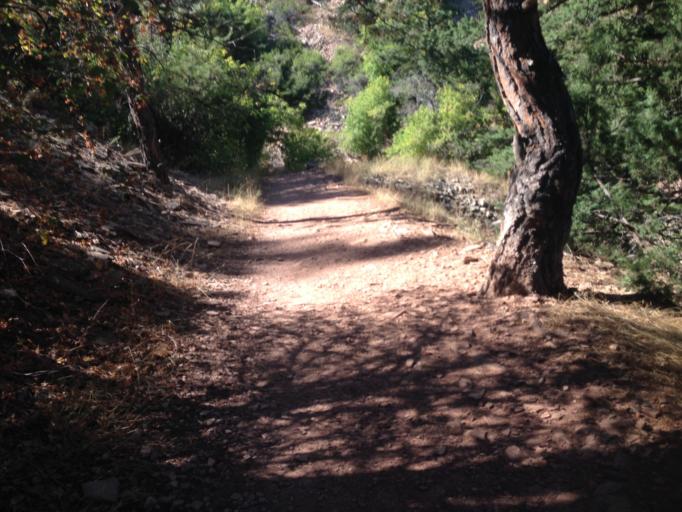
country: US
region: Colorado
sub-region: Boulder County
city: Boulder
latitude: 39.9840
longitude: -105.2874
